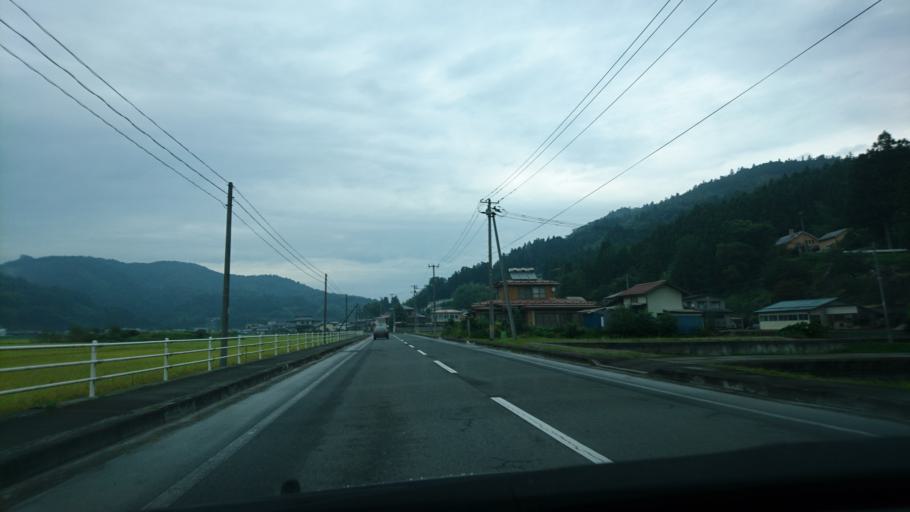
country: JP
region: Iwate
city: Ichinoseki
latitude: 38.9712
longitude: 141.2442
